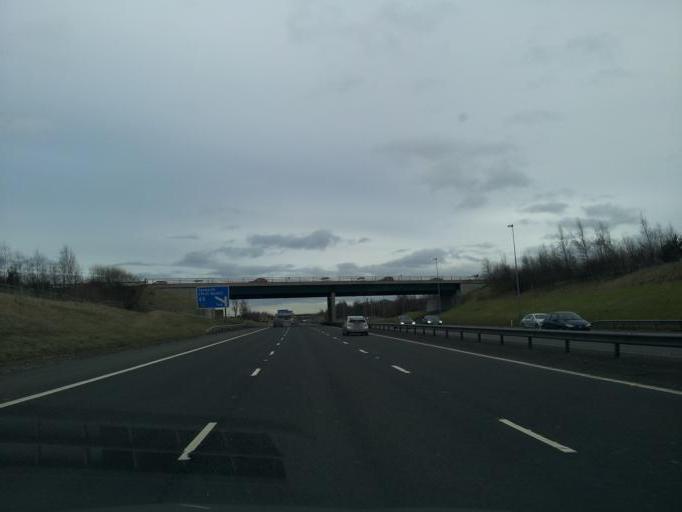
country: GB
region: England
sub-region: Staffordshire
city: Shenstone
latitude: 52.6482
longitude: -1.8358
